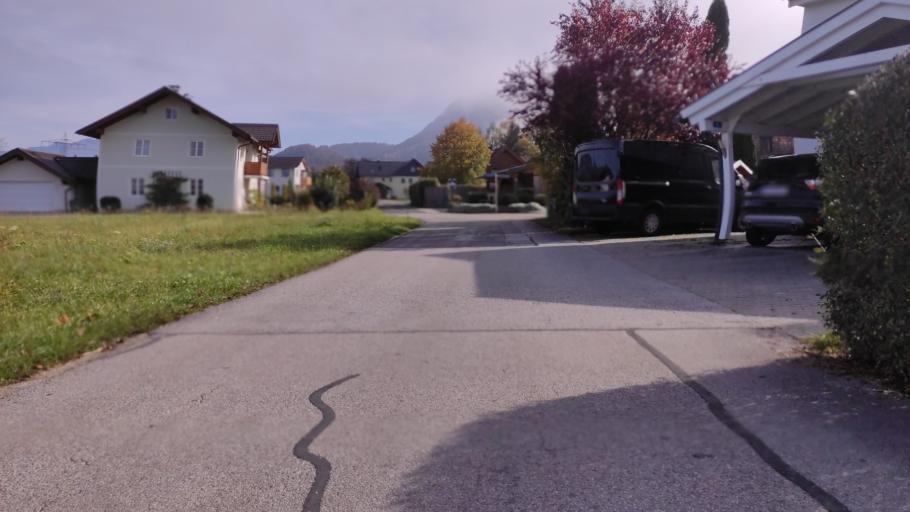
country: AT
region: Salzburg
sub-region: Politischer Bezirk Salzburg-Umgebung
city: Strobl
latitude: 47.7145
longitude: 13.4918
